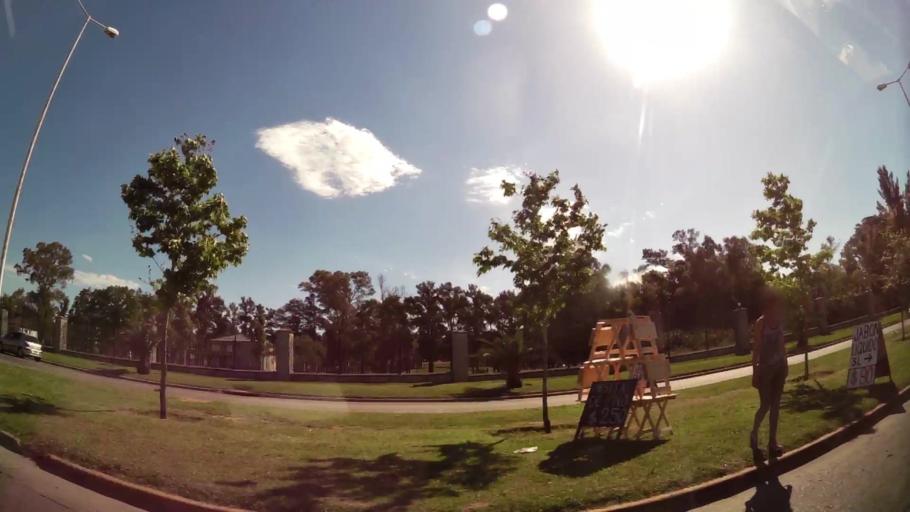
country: AR
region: Buenos Aires
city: Hurlingham
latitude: -34.4944
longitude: -58.6960
